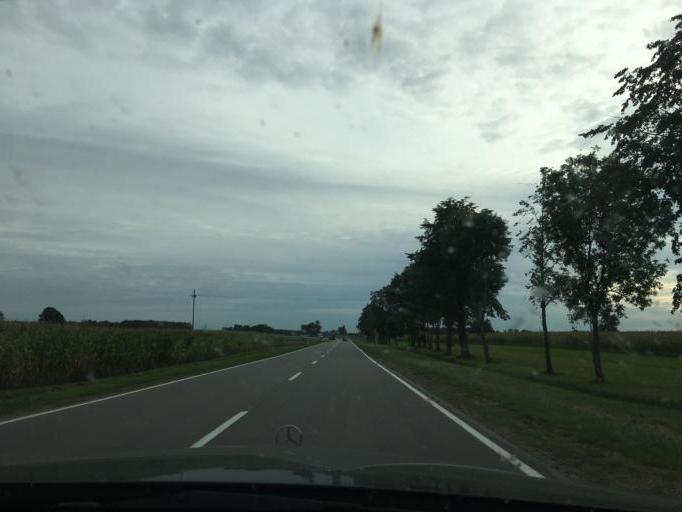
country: PL
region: Masovian Voivodeship
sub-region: Powiat ostrowski
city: Ostrow Mazowiecka
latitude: 52.8879
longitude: 21.8658
